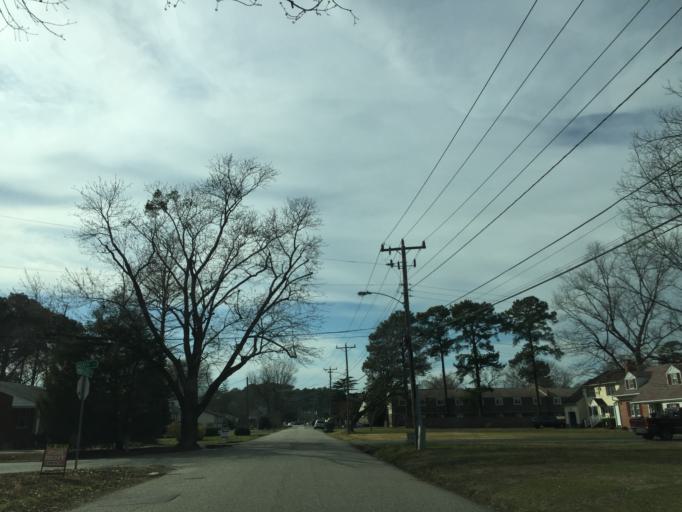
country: US
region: Virginia
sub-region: City of Newport News
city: Newport News
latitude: 37.0757
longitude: -76.4911
